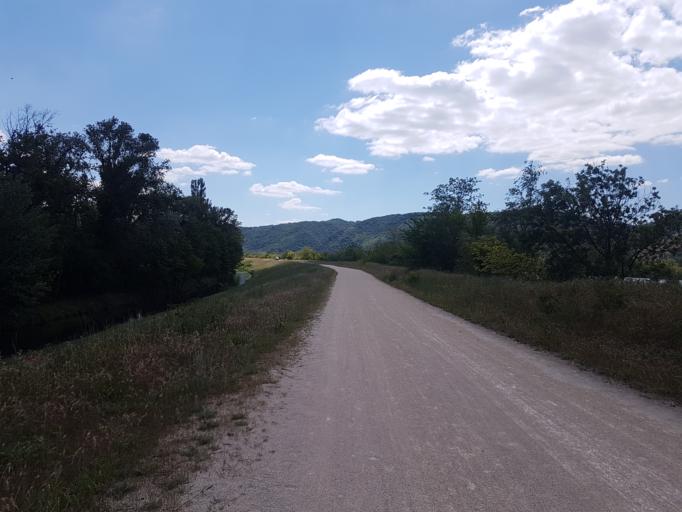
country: FR
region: Rhone-Alpes
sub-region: Departement de l'Ardeche
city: Mauves
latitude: 45.0368
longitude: 4.8440
